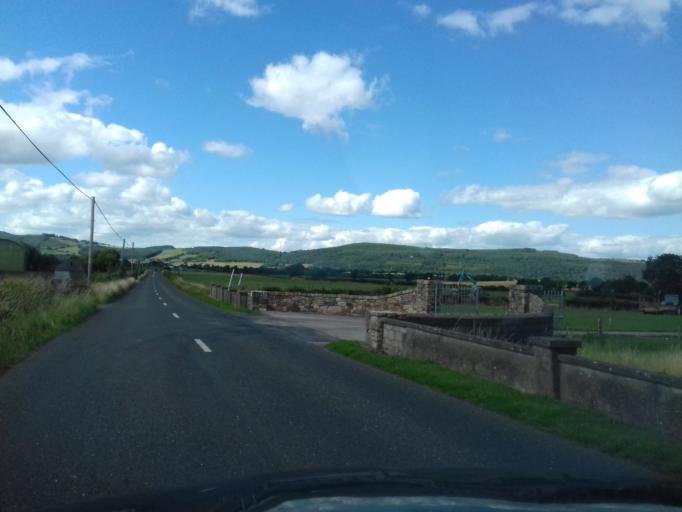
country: IE
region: Munster
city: Carrick-on-Suir
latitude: 52.3715
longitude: -7.4482
